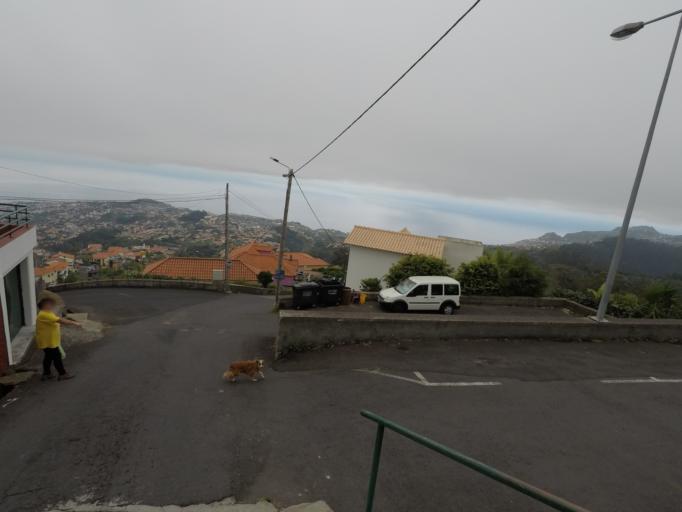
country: PT
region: Madeira
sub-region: Camara de Lobos
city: Curral das Freiras
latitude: 32.6861
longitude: -16.9482
